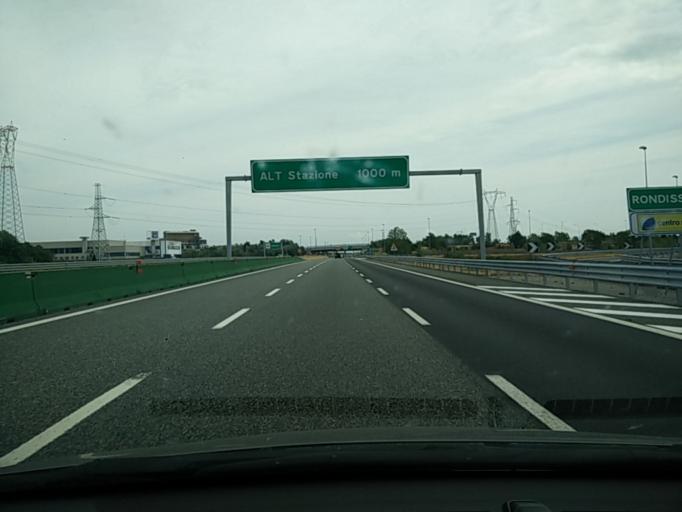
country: IT
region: Piedmont
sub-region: Provincia di Torino
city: Rondissone
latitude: 45.2348
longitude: 7.9512
